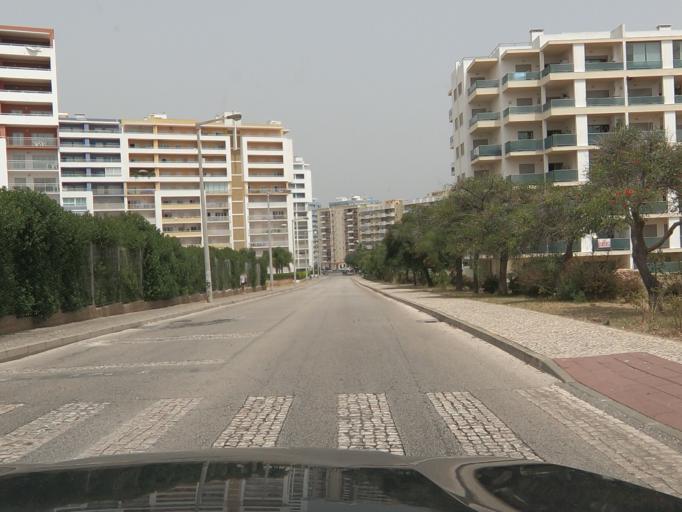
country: PT
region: Faro
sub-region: Portimao
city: Portimao
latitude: 37.1291
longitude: -8.5432
